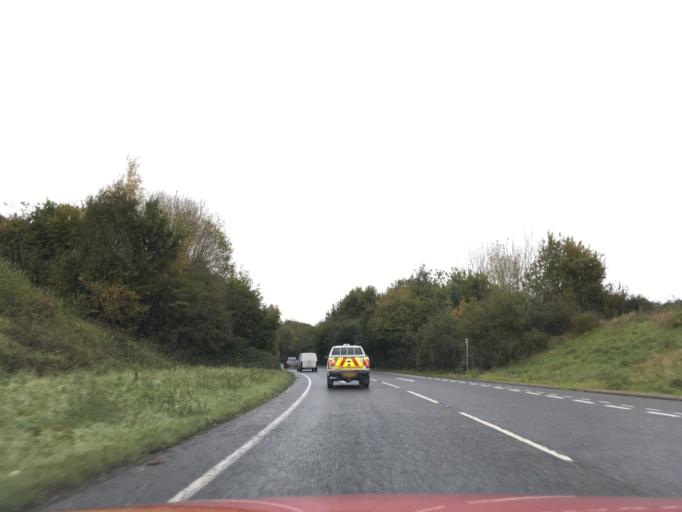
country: GB
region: England
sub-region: Hampshire
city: Eastleigh
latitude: 50.9887
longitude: -1.3504
